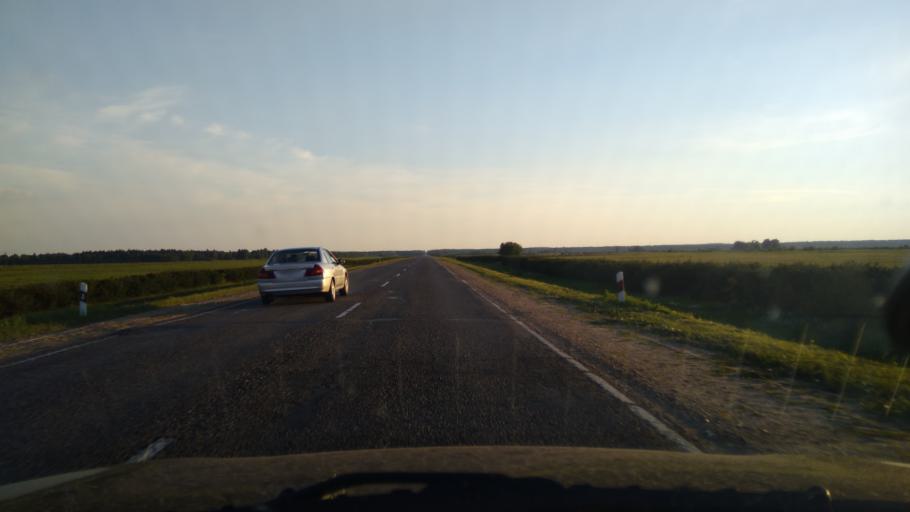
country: BY
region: Brest
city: Nyakhachava
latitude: 52.6340
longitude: 25.1852
